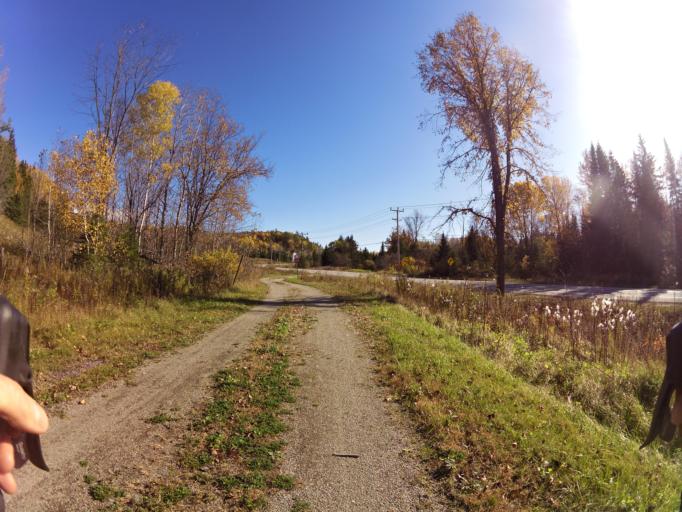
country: CA
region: Quebec
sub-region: Outaouais
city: Wakefield
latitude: 45.8442
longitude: -75.9800
